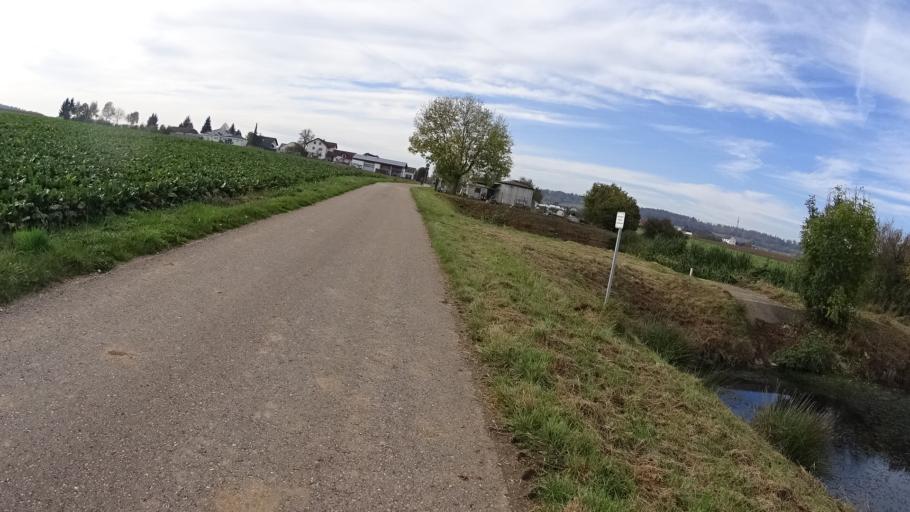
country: DE
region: Bavaria
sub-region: Upper Bavaria
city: Adelschlag
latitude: 48.8569
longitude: 11.2474
